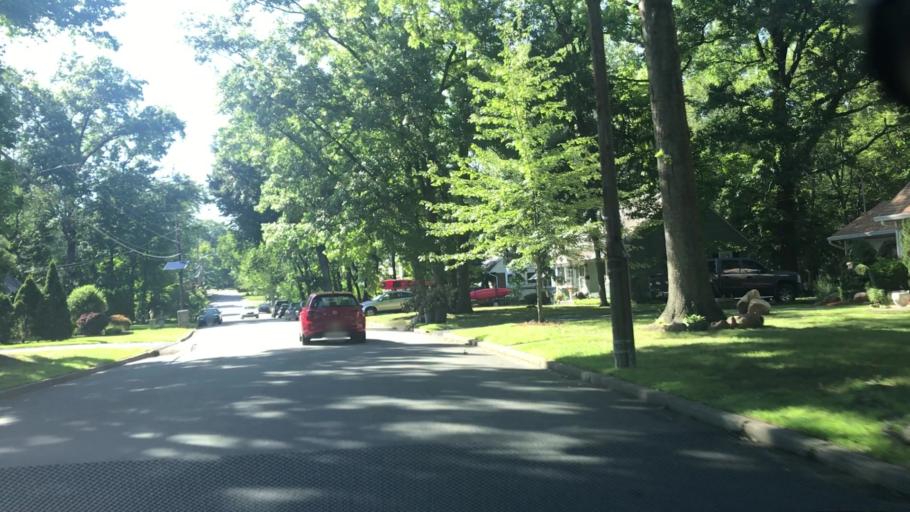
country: US
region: New Jersey
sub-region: Bergen County
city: Maywood
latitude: 40.9196
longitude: -74.0574
